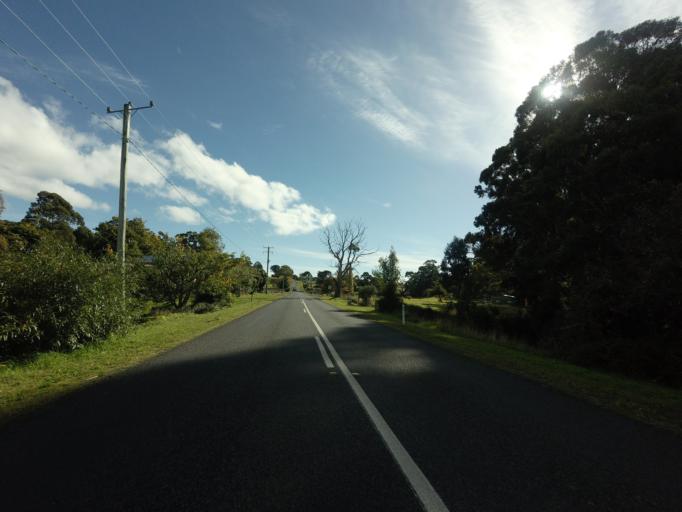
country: AU
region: Tasmania
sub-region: Clarence
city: Sandford
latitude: -43.0610
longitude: 147.8114
